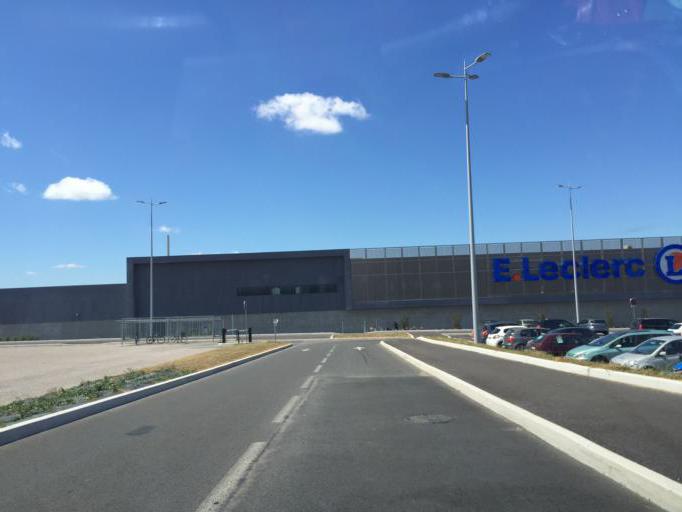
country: FR
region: Auvergne
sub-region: Departement de l'Allier
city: Moulins
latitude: 46.5884
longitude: 3.3322
